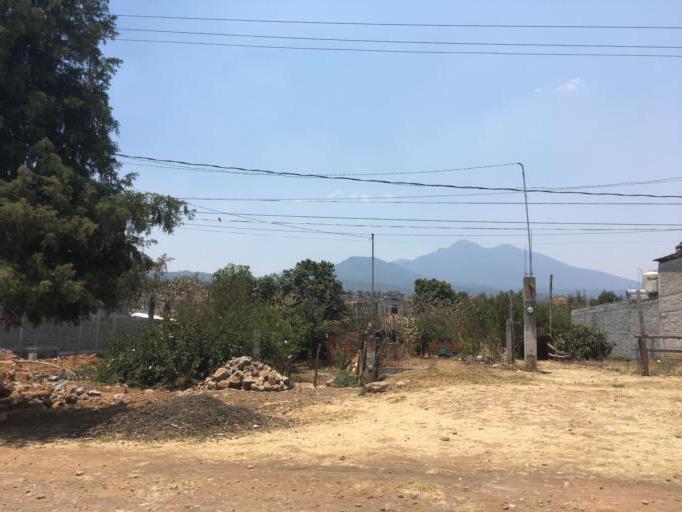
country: MX
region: Michoacan
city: Santa Fe de la Laguna
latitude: 19.6701
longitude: -101.5533
